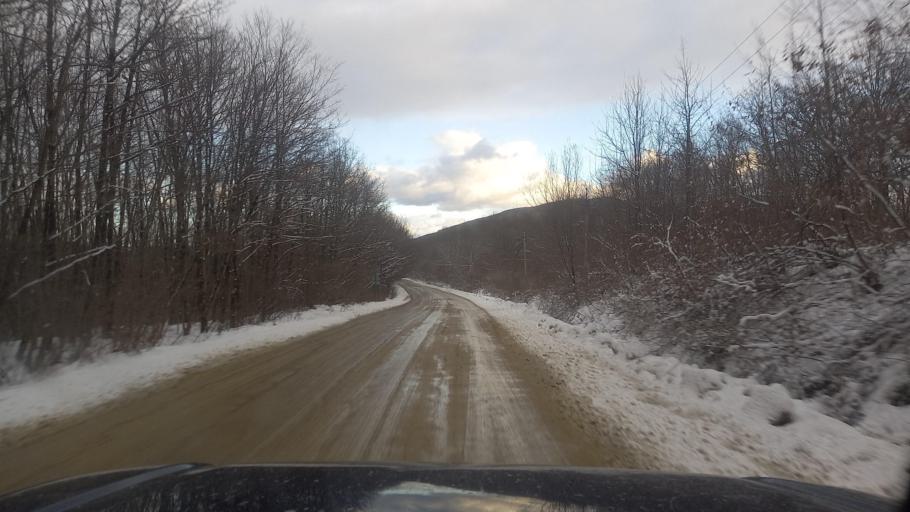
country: RU
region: Krasnodarskiy
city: Smolenskaya
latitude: 44.6758
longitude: 38.7347
